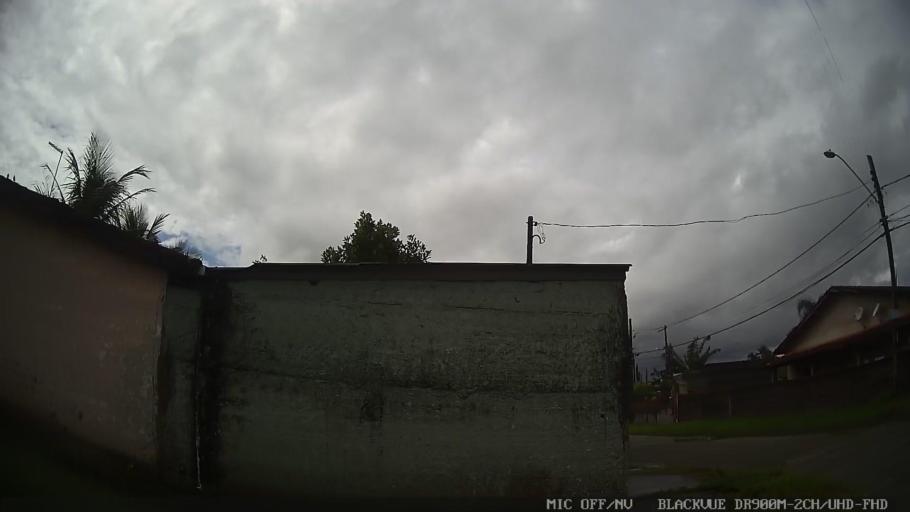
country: BR
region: Sao Paulo
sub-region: Itanhaem
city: Itanhaem
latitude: -24.1605
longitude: -46.7937
